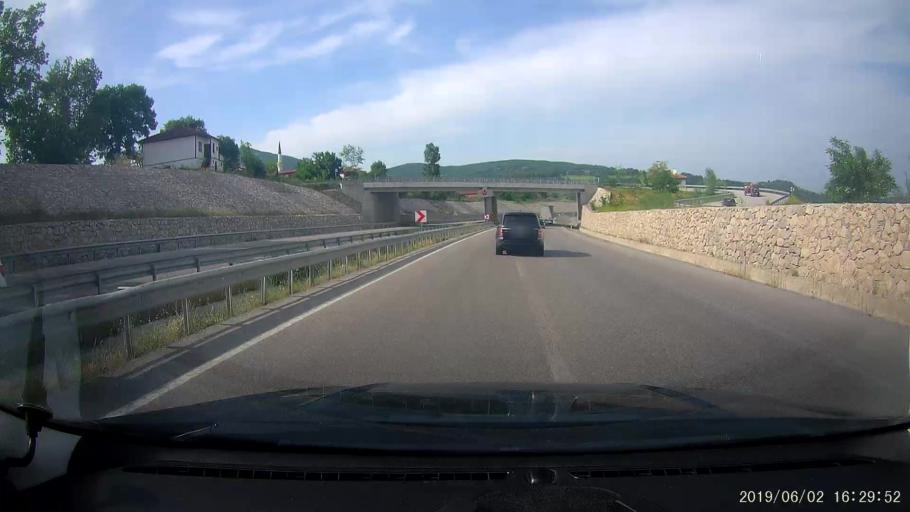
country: TR
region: Samsun
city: Ladik
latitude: 41.0190
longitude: 35.8728
